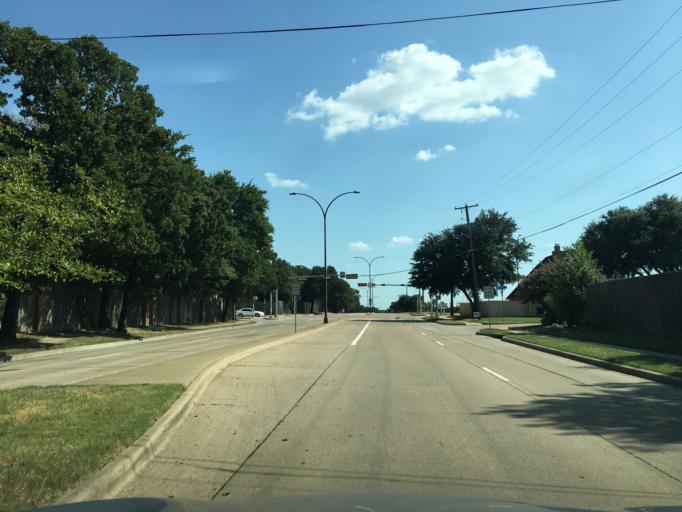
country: US
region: Texas
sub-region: Tarrant County
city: Dalworthington Gardens
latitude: 32.6710
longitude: -97.1497
